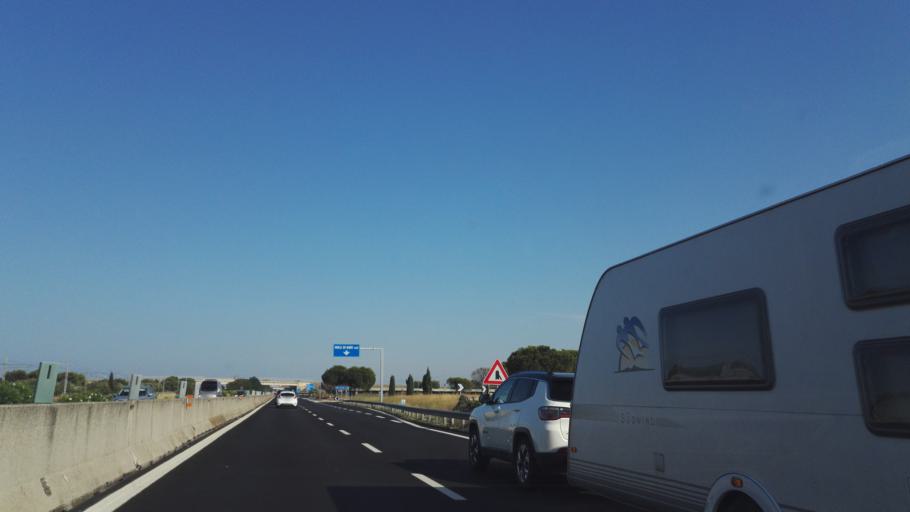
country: IT
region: Apulia
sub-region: Provincia di Bari
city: Mola di Bari
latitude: 41.0457
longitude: 17.1056
